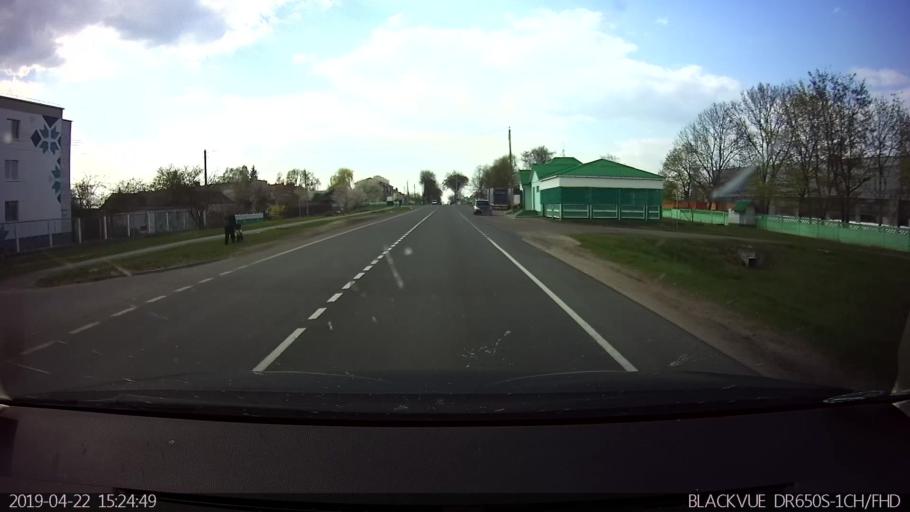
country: BY
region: Brest
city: Vysokaye
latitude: 52.3624
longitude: 23.4028
